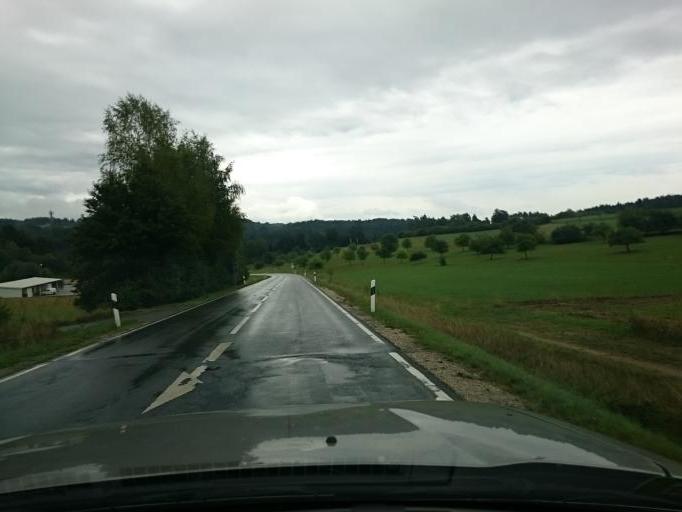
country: DE
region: Bavaria
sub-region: Upper Franconia
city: Pottenstein
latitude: 49.7618
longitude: 11.4056
